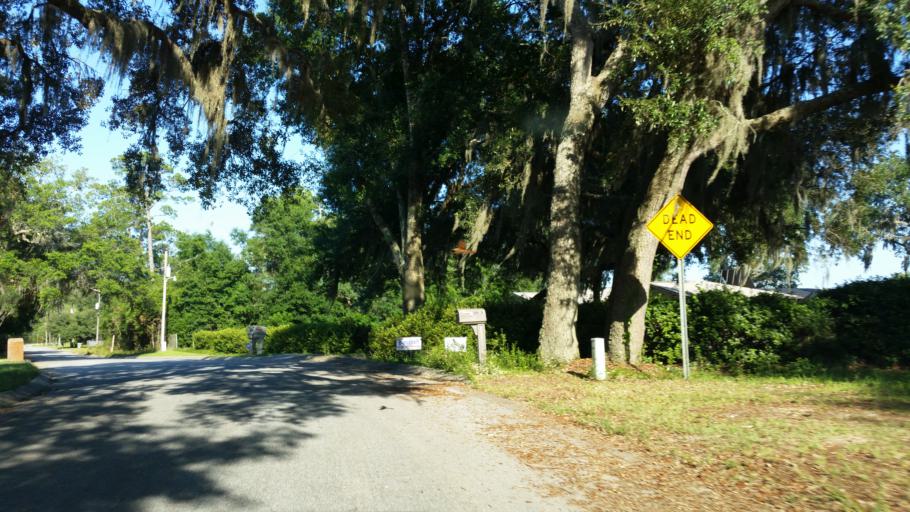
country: US
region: Florida
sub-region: Escambia County
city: Bellview
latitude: 30.4602
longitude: -87.4092
